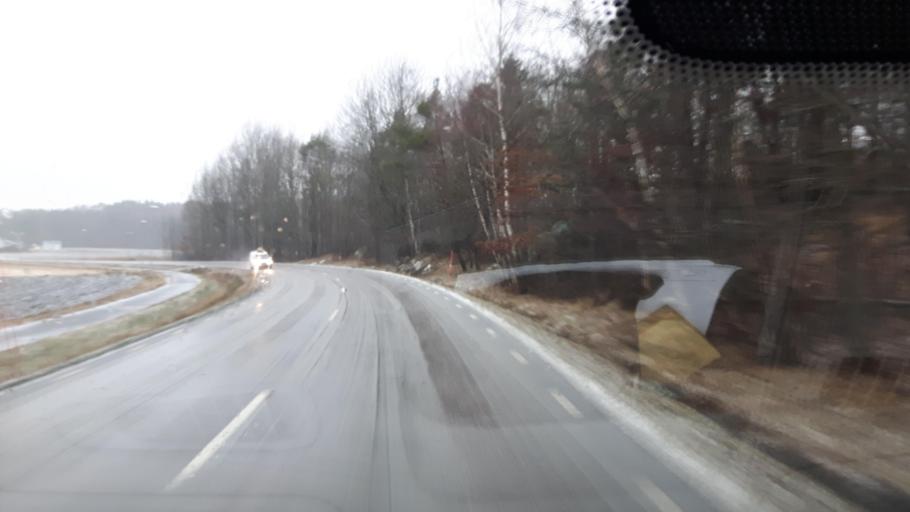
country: SE
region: Halland
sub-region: Kungsbacka Kommun
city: Vallda
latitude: 57.4597
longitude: 11.9797
